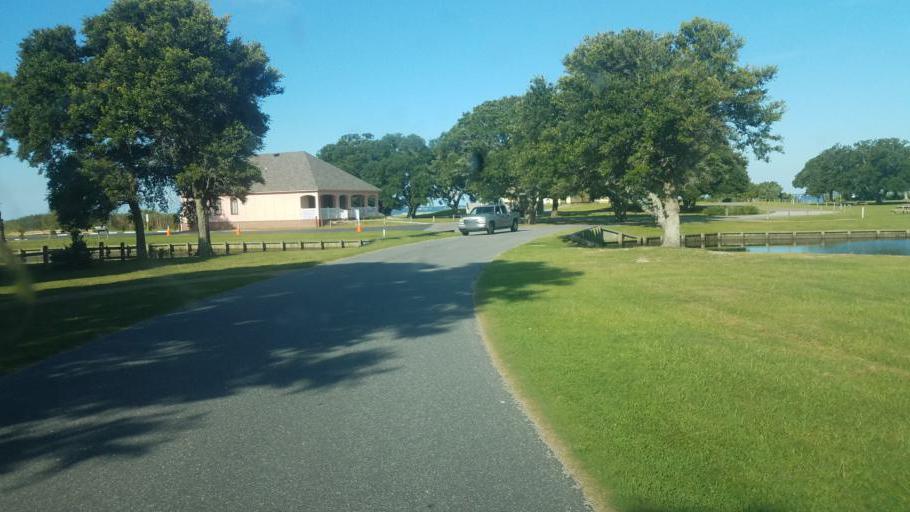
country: US
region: North Carolina
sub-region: Currituck County
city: Currituck
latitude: 36.3738
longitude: -75.8308
